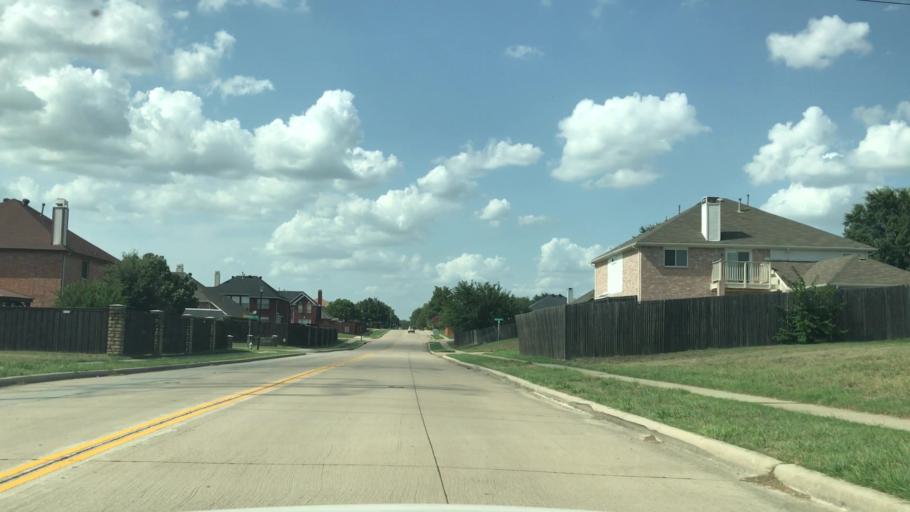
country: US
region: Texas
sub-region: Dallas County
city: Carrollton
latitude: 32.9764
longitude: -96.8643
